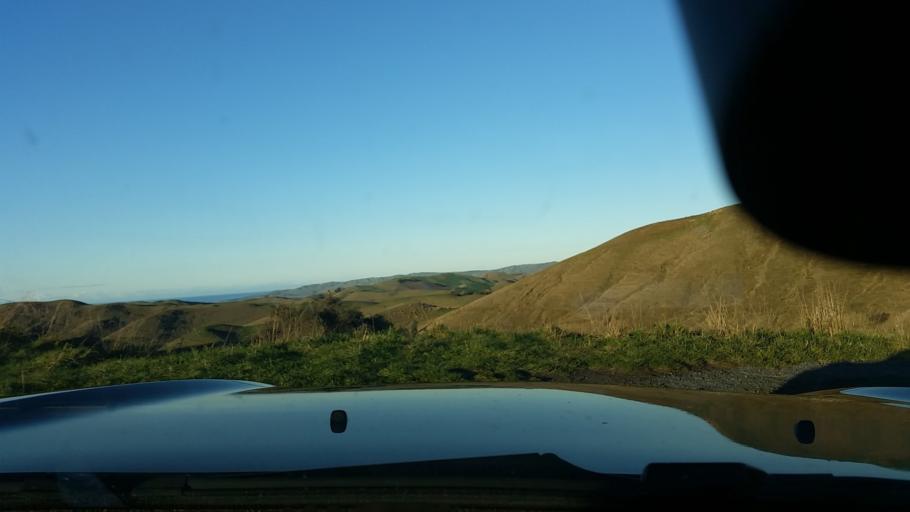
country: NZ
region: Marlborough
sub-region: Marlborough District
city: Blenheim
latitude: -41.7481
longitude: 174.0581
